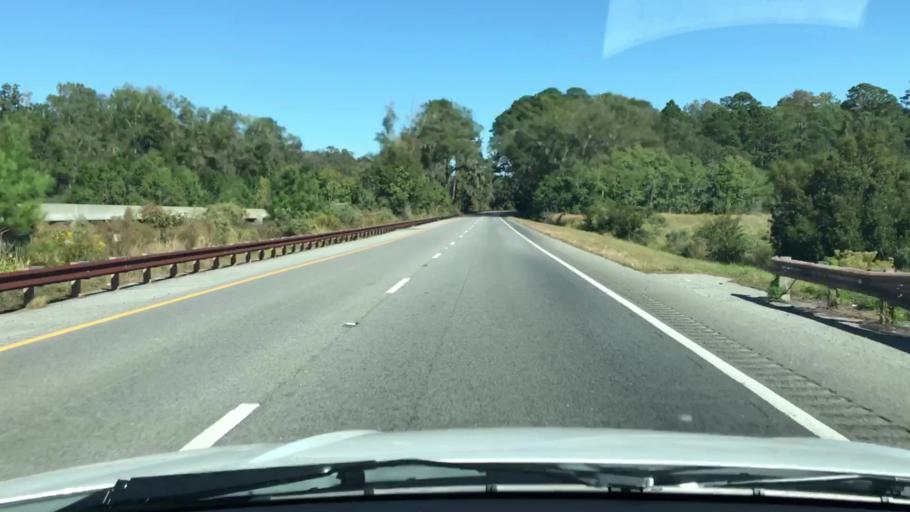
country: US
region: South Carolina
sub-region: Hampton County
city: Yemassee
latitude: 32.6476
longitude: -80.6973
